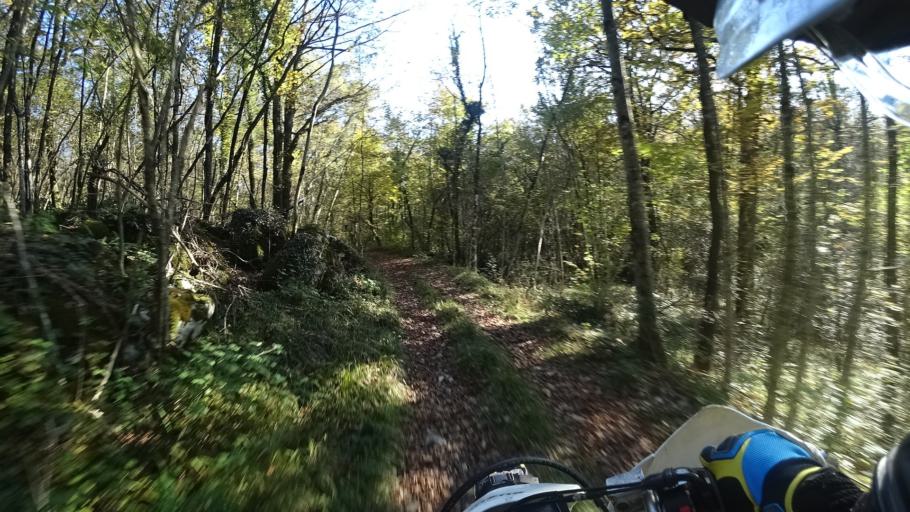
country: HR
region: Primorsko-Goranska
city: Matulji
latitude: 45.3914
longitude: 14.2952
